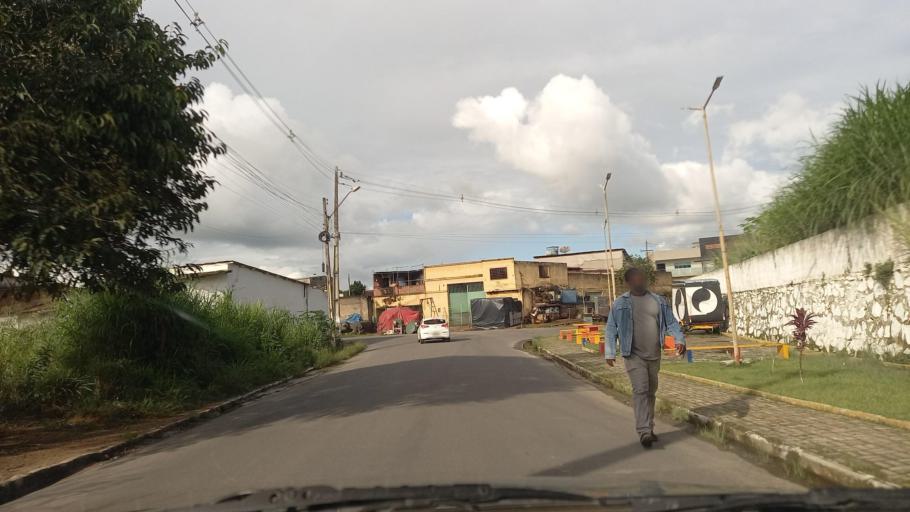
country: BR
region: Pernambuco
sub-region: Palmares
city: Palmares
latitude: -8.6784
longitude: -35.5803
